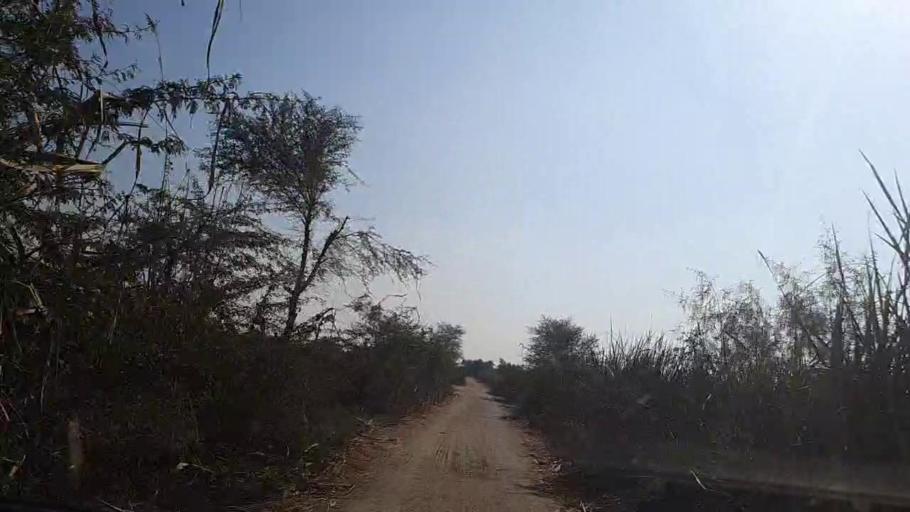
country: PK
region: Sindh
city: Sakrand
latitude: 26.0771
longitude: 68.3694
